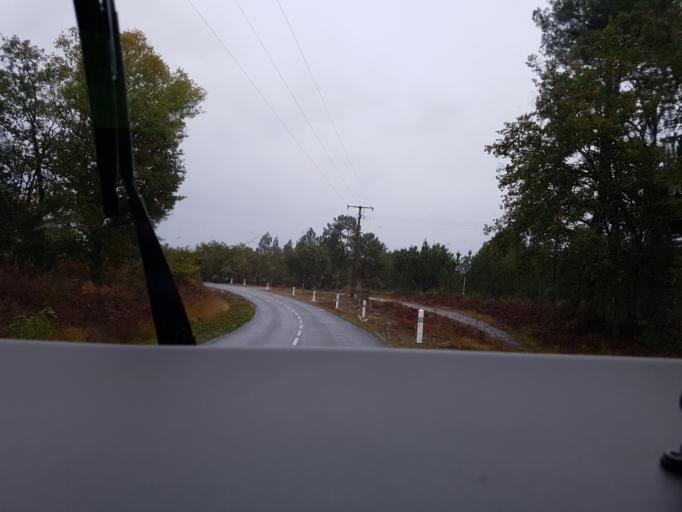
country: FR
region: Aquitaine
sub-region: Departement des Landes
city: Pissos
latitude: 44.3730
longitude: -0.6470
